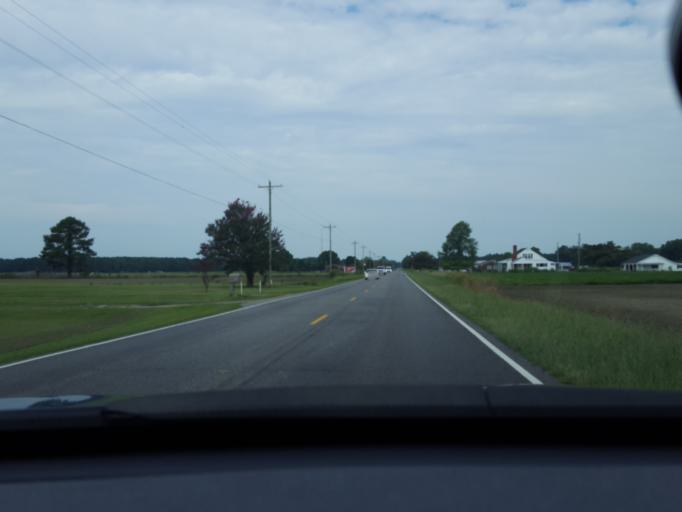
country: US
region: North Carolina
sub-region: Chowan County
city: Edenton
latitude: 36.1145
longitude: -76.6435
